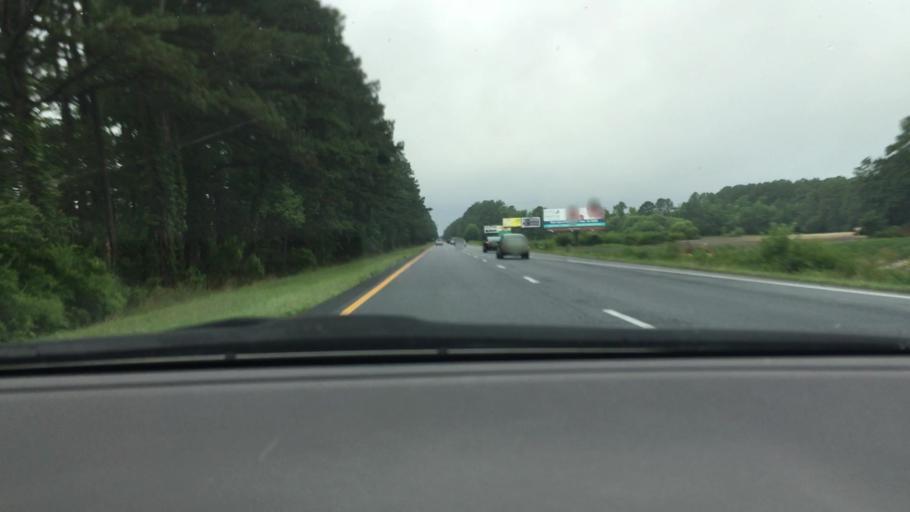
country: US
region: Maryland
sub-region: Wicomico County
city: Fruitland
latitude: 38.2800
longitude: -75.6518
